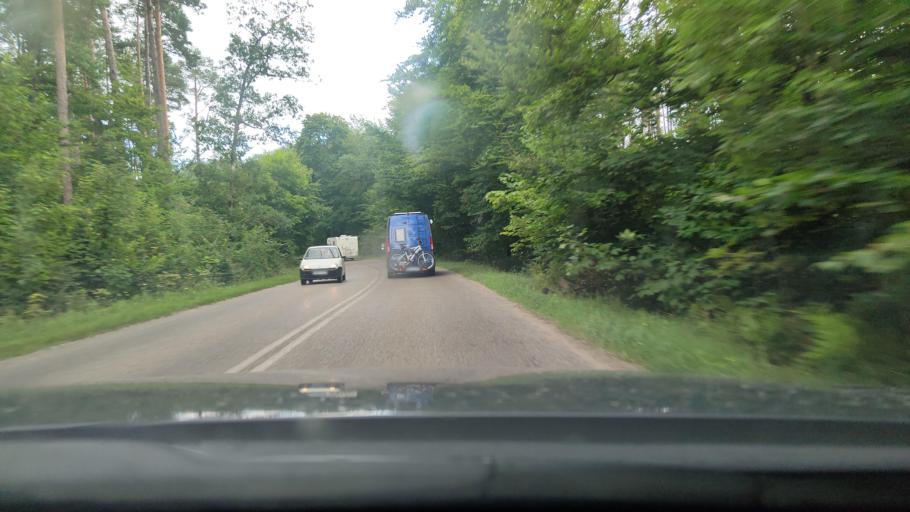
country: PL
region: Pomeranian Voivodeship
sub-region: Powiat wejherowski
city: Orle
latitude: 54.7056
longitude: 18.1679
